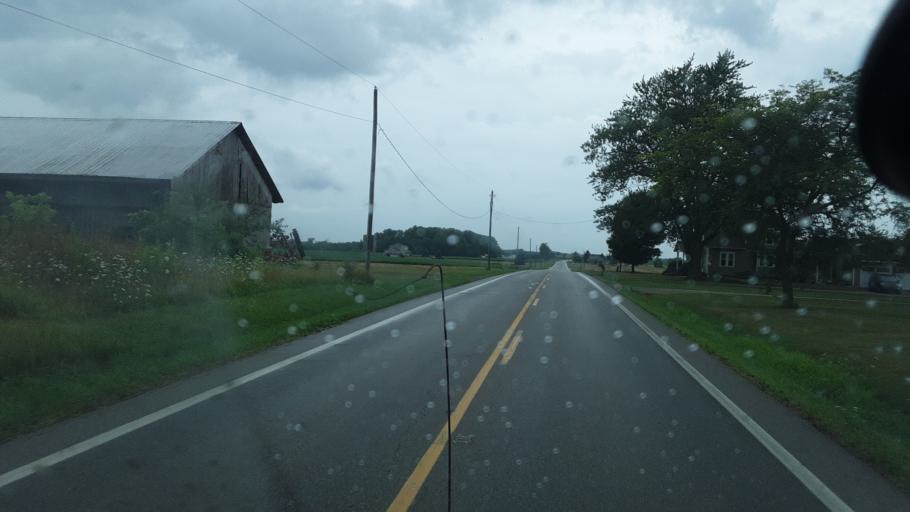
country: US
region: Ohio
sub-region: Williams County
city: Edgerton
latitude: 41.5564
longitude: -84.7949
